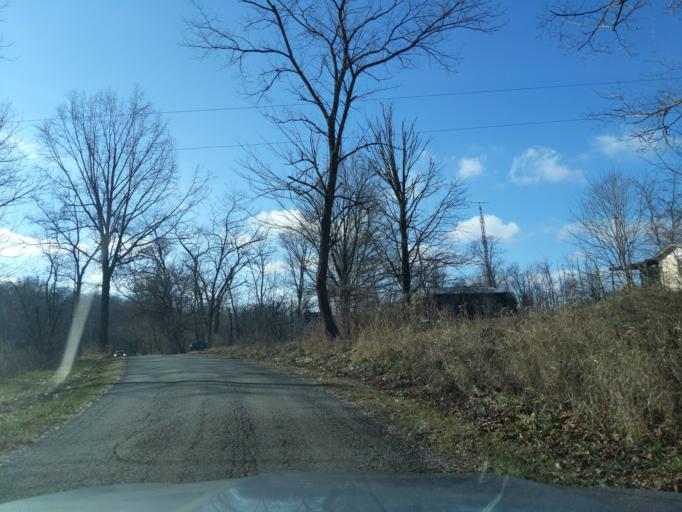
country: US
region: Indiana
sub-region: Decatur County
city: Greensburg
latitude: 39.2424
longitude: -85.4636
